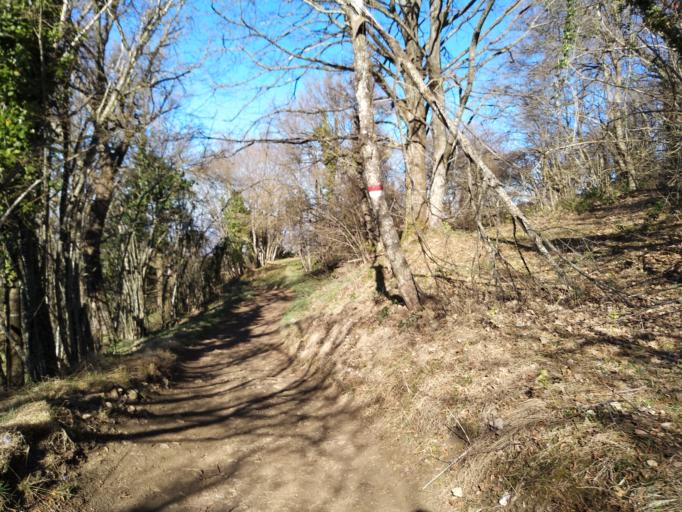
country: IT
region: Emilia-Romagna
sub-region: Provincia di Reggio Emilia
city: Castelnovo ne'Monti
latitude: 44.4235
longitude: 10.4145
